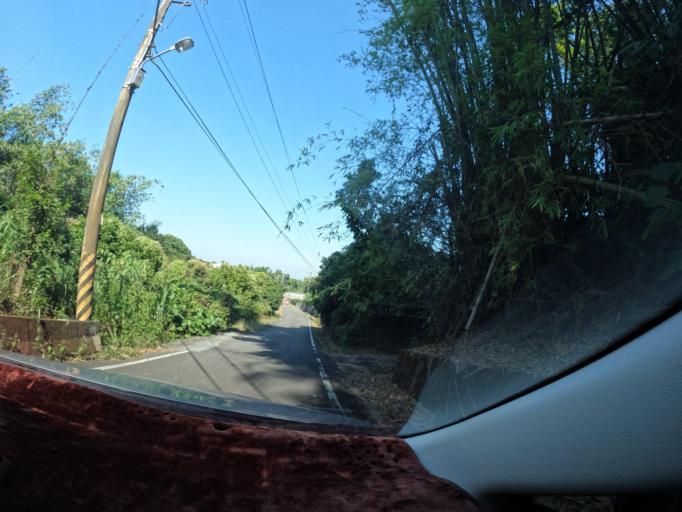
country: TW
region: Taiwan
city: Yujing
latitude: 23.0624
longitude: 120.3814
